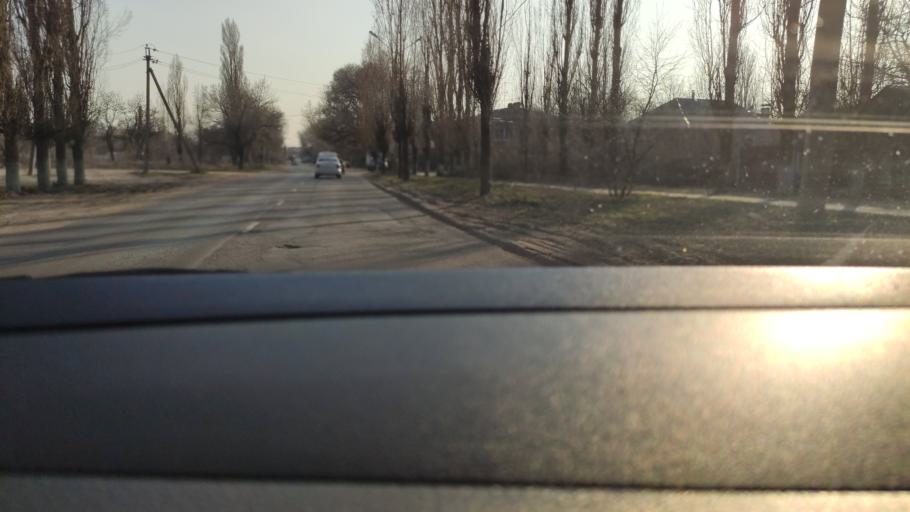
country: RU
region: Voronezj
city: Maslovka
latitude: 51.5837
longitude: 39.3186
